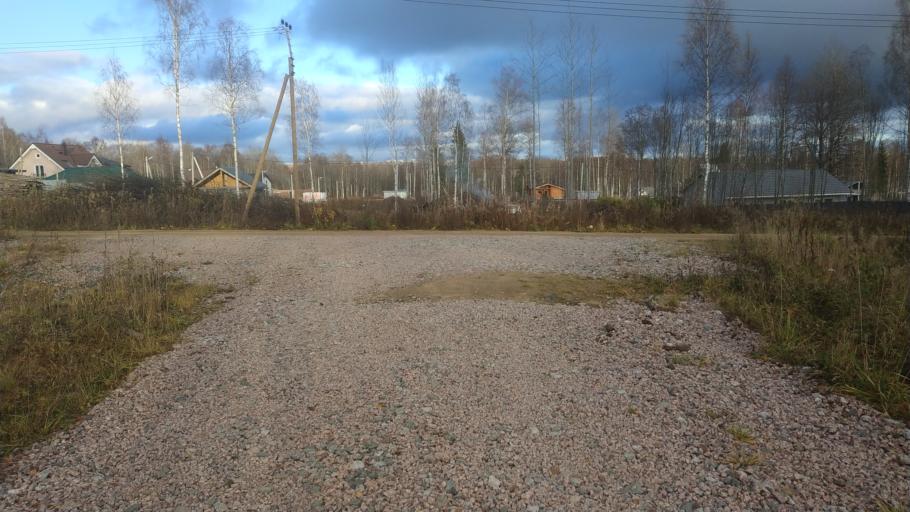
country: RU
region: Leningrad
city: Agalatovo
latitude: 60.3251
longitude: 30.2321
